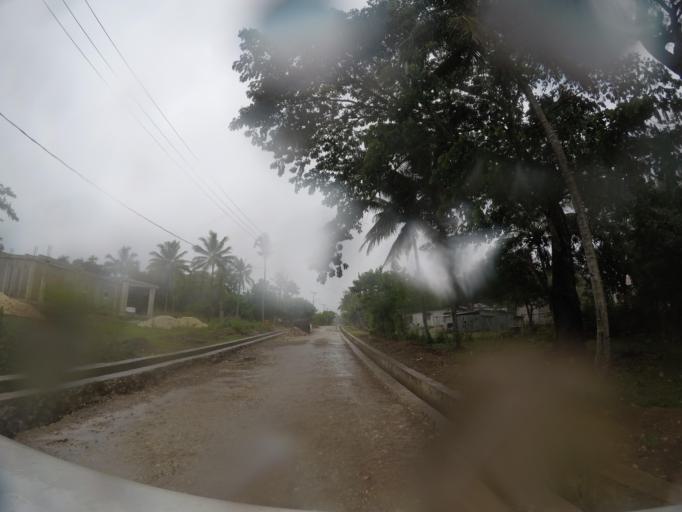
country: TL
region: Lautem
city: Lospalos
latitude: -8.5162
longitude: 127.0073
